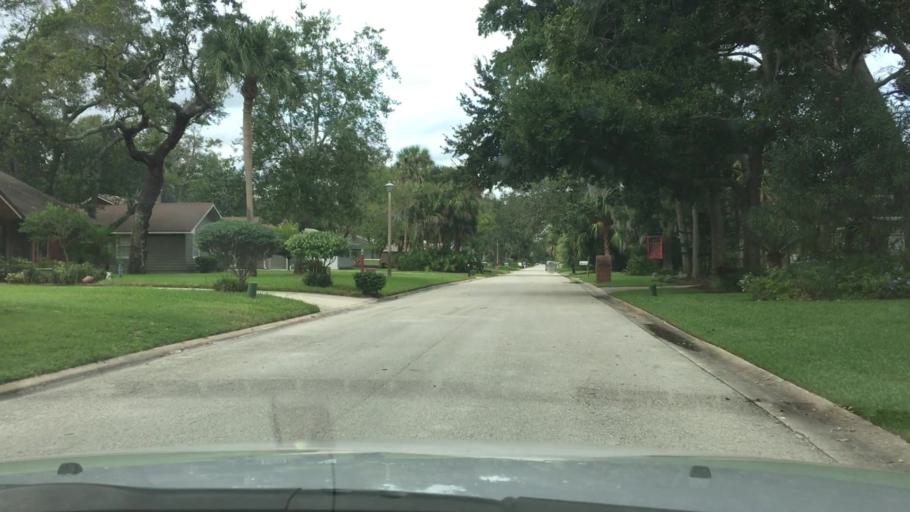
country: US
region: Florida
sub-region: Volusia County
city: Ormond-by-the-Sea
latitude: 29.3185
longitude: -81.0712
